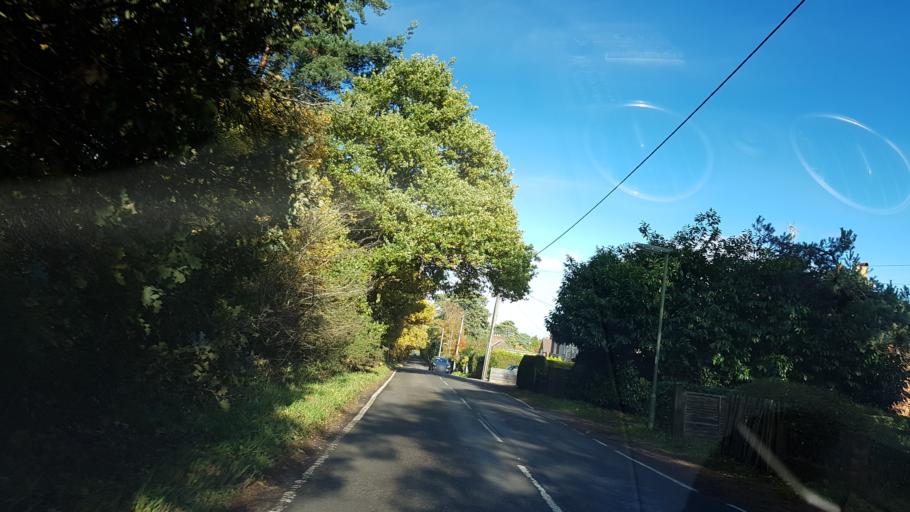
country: GB
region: England
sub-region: Surrey
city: Elstead
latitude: 51.1704
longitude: -0.7143
